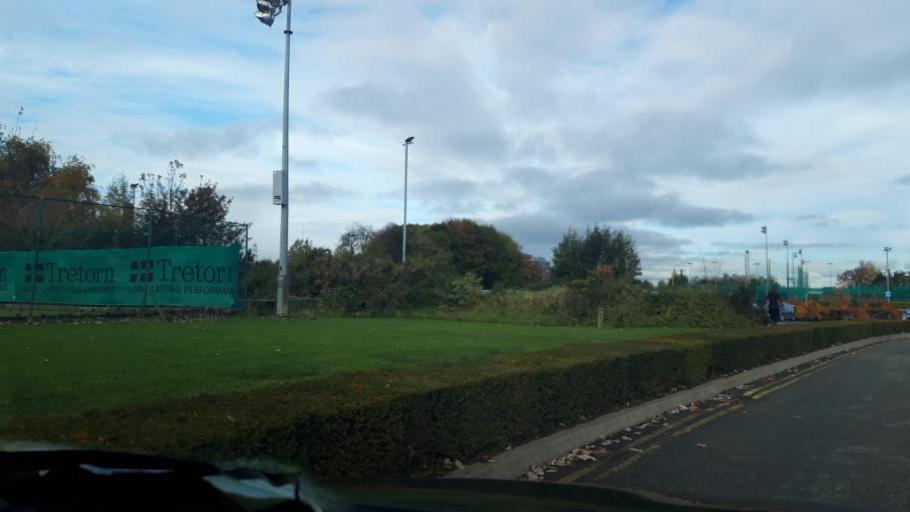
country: IE
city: Clonskeagh
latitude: 53.3081
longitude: -6.2304
